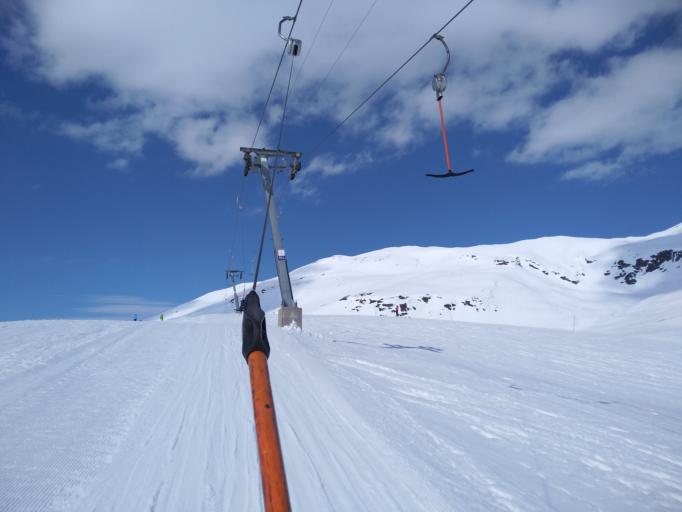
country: NO
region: Sogn og Fjordane
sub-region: Vik
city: Vik
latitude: 60.8655
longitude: 6.4557
